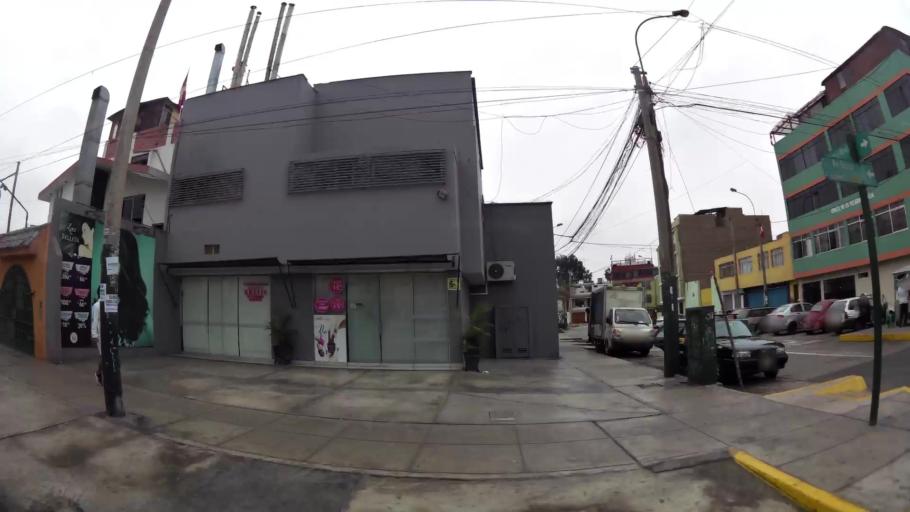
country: PE
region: Lima
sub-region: Lima
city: Surco
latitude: -12.1403
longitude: -76.9944
